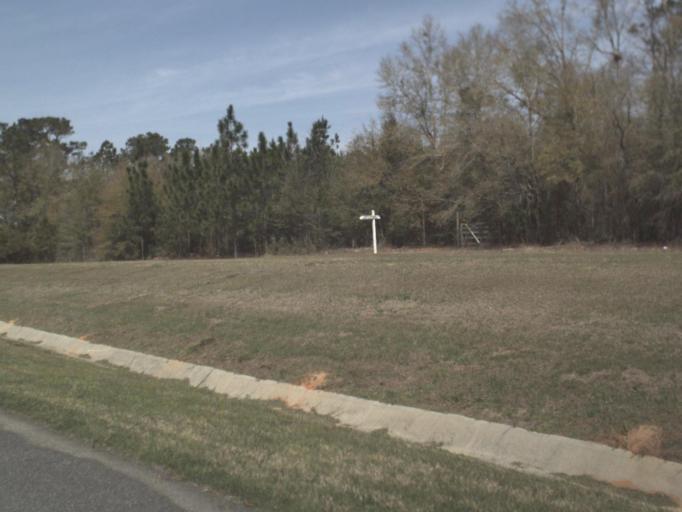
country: US
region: Florida
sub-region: Walton County
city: DeFuniak Springs
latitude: 30.7230
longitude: -85.9526
